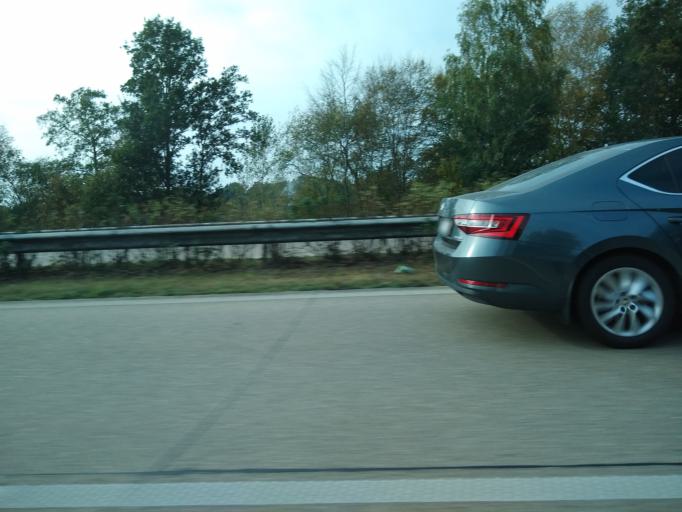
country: DE
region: Lower Saxony
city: Oldenburg
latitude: 53.1331
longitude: 8.2763
